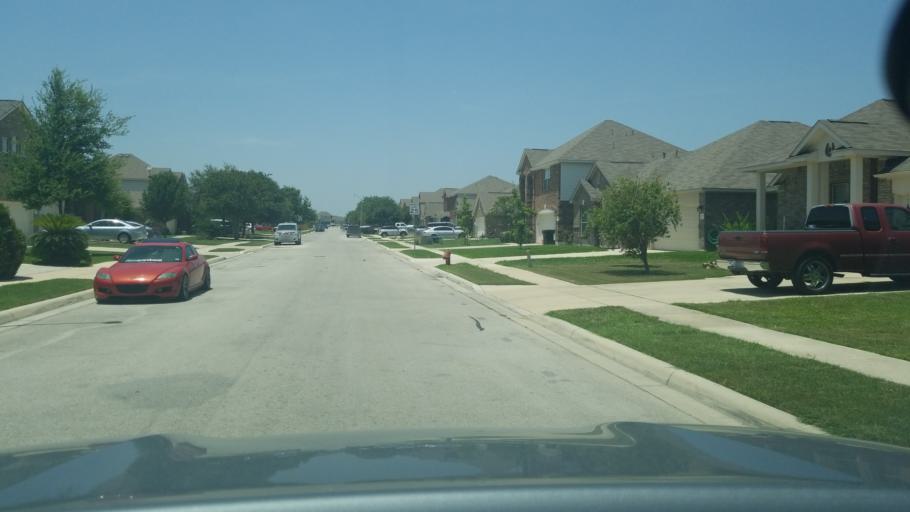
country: US
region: Texas
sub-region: Guadalupe County
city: Cibolo
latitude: 29.5750
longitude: -98.2281
